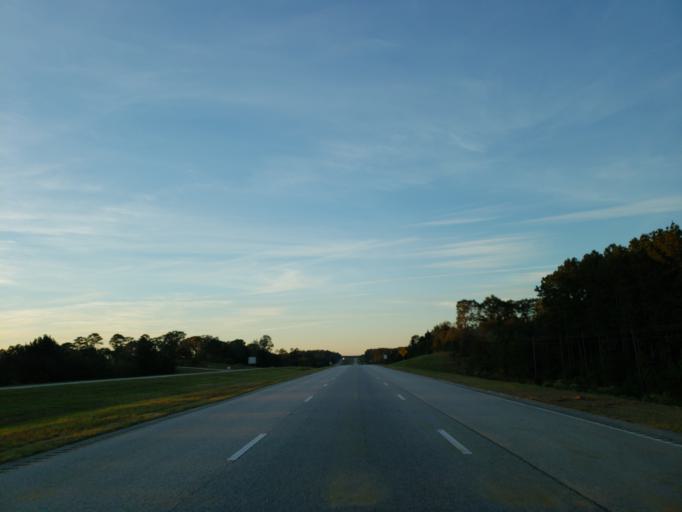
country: US
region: Mississippi
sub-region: Wayne County
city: Belmont
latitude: 31.4622
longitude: -88.4700
